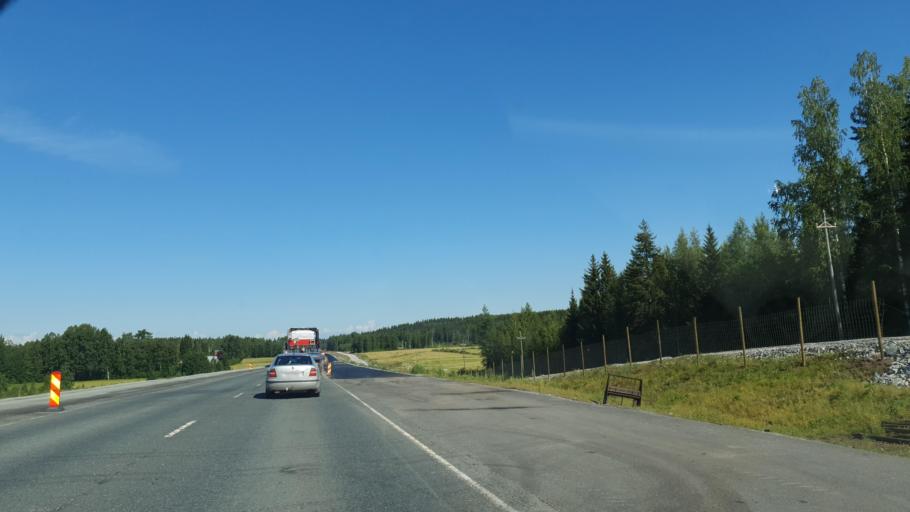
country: FI
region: Northern Savo
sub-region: Ylae-Savo
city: Lapinlahti
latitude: 63.2831
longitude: 27.4556
